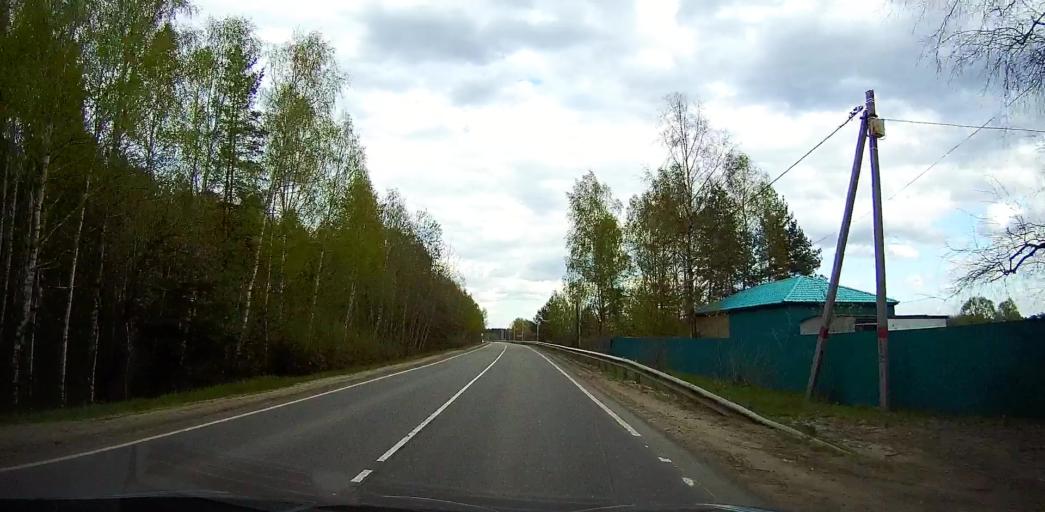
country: RU
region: Moskovskaya
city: Pavlovskiy Posad
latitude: 55.8011
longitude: 38.6585
